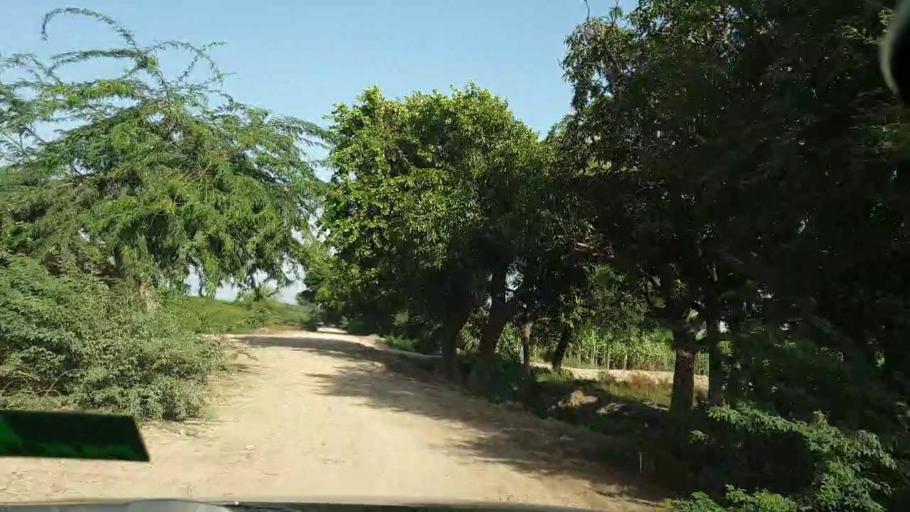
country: PK
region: Sindh
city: Naukot
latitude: 24.7029
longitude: 69.2172
